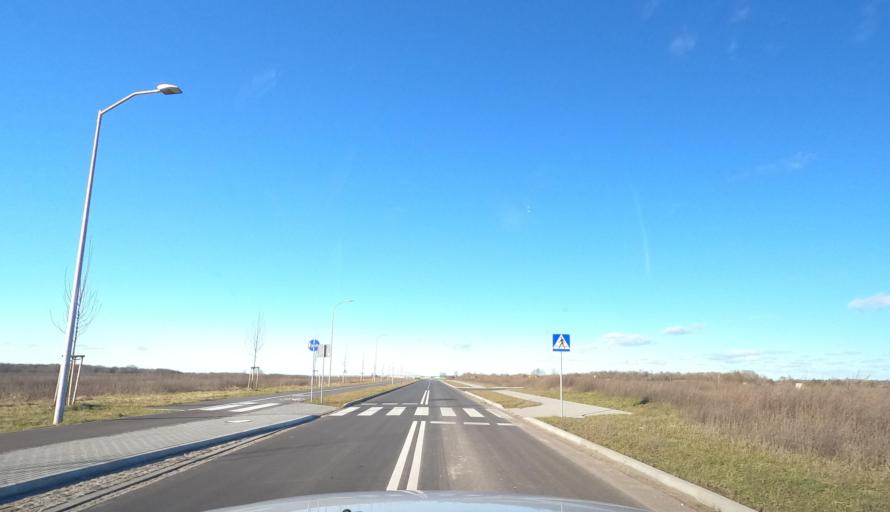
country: PL
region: West Pomeranian Voivodeship
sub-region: Powiat pyrzycki
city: Warnice
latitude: 53.2692
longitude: 14.9857
